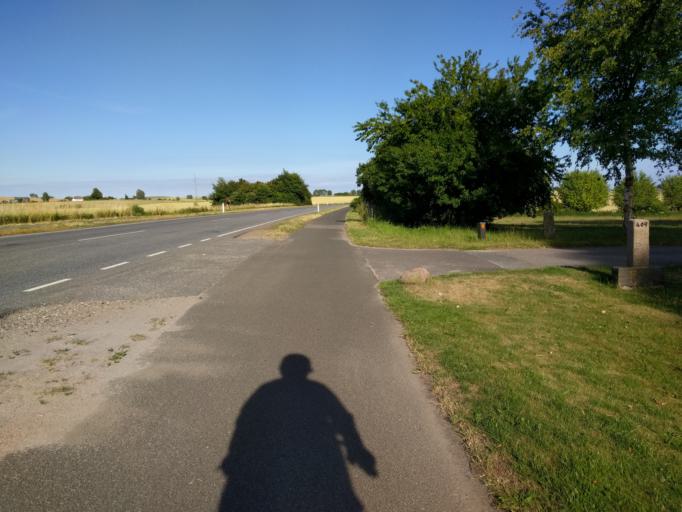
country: DK
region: South Denmark
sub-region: Kerteminde Kommune
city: Munkebo
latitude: 55.4607
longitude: 10.6013
